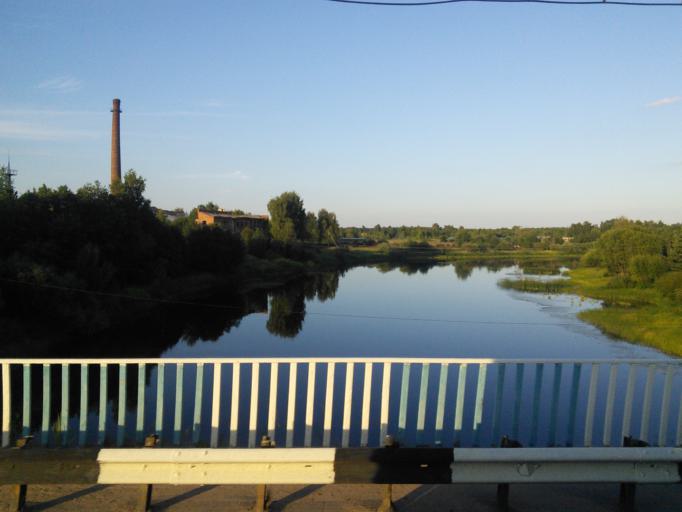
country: RU
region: Vologda
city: Chagoda
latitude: 59.1595
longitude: 35.3318
